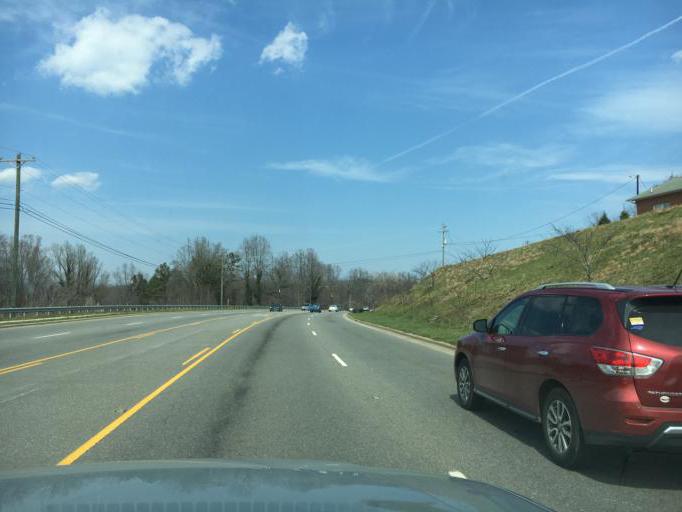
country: US
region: North Carolina
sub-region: McDowell County
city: West Marion
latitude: 35.6610
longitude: -82.0245
